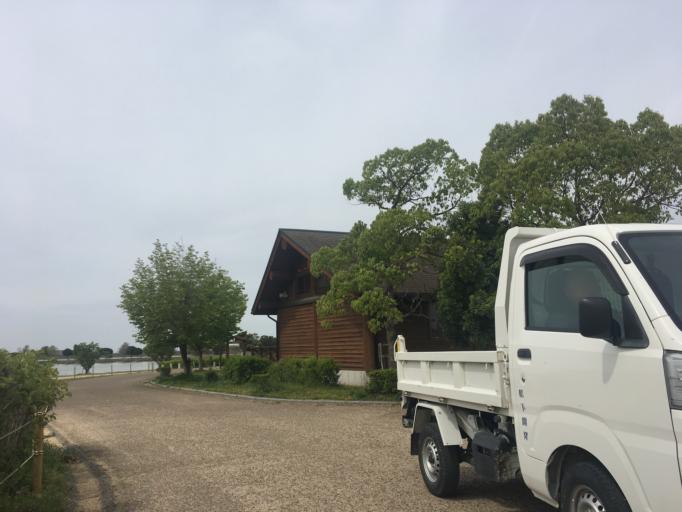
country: JP
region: Hyogo
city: Miki
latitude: 34.7669
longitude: 134.9253
